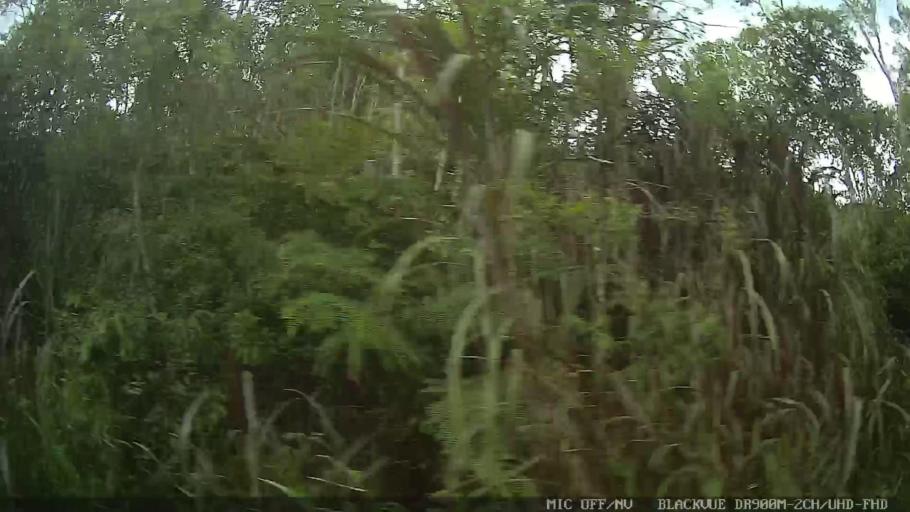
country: BR
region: Sao Paulo
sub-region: Rio Grande Da Serra
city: Rio Grande da Serra
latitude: -23.7030
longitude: -46.2724
